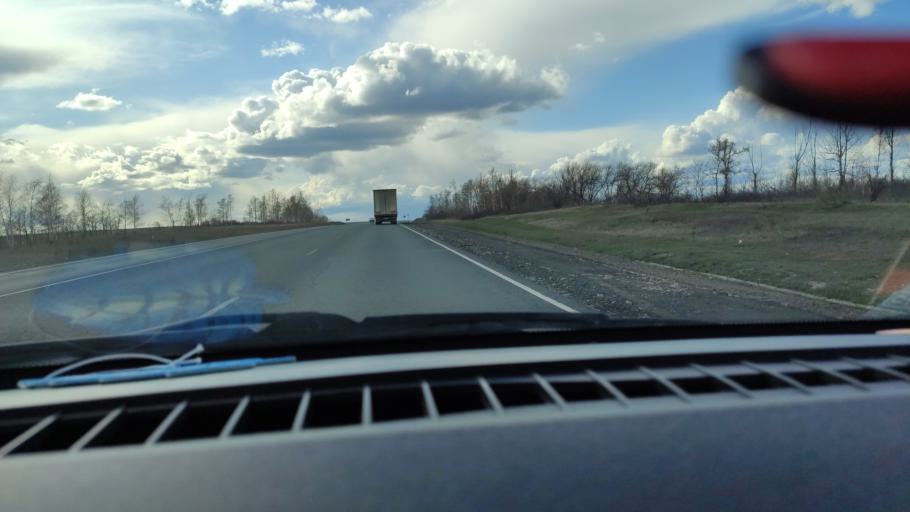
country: RU
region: Saratov
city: Shikhany
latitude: 52.1224
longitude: 47.2567
